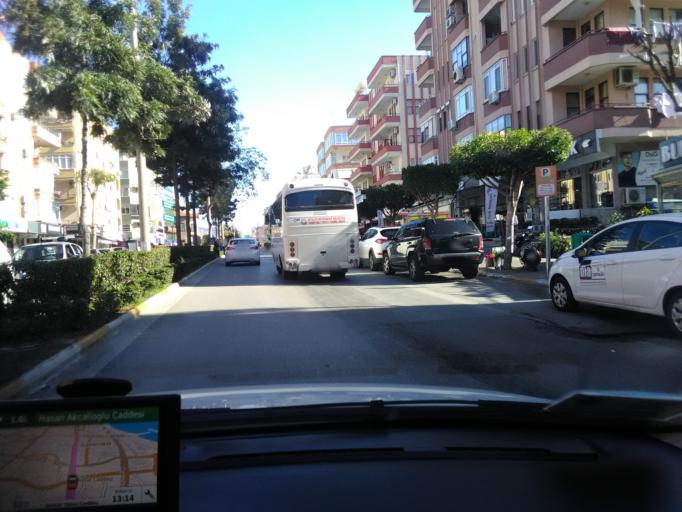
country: TR
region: Antalya
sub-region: Alanya
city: Alanya
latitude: 36.5473
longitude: 31.9951
